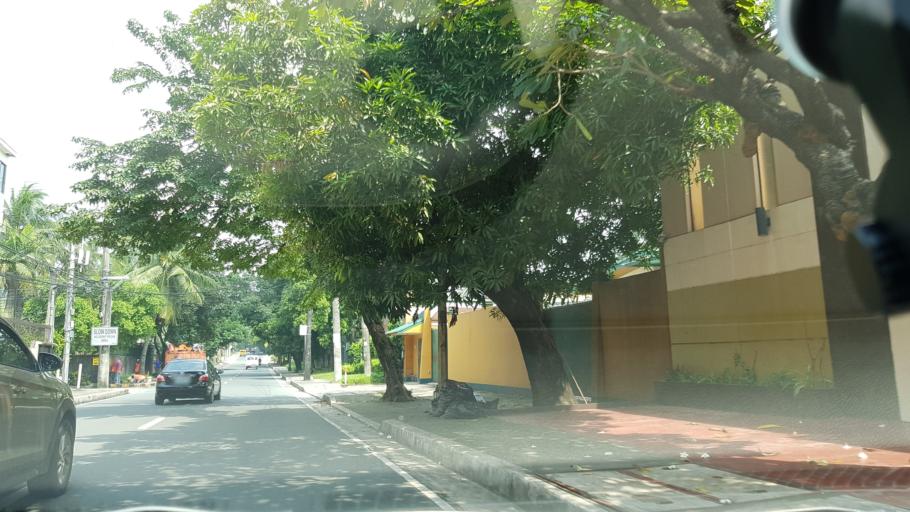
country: PH
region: Metro Manila
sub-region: San Juan
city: San Juan
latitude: 14.6193
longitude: 121.0344
